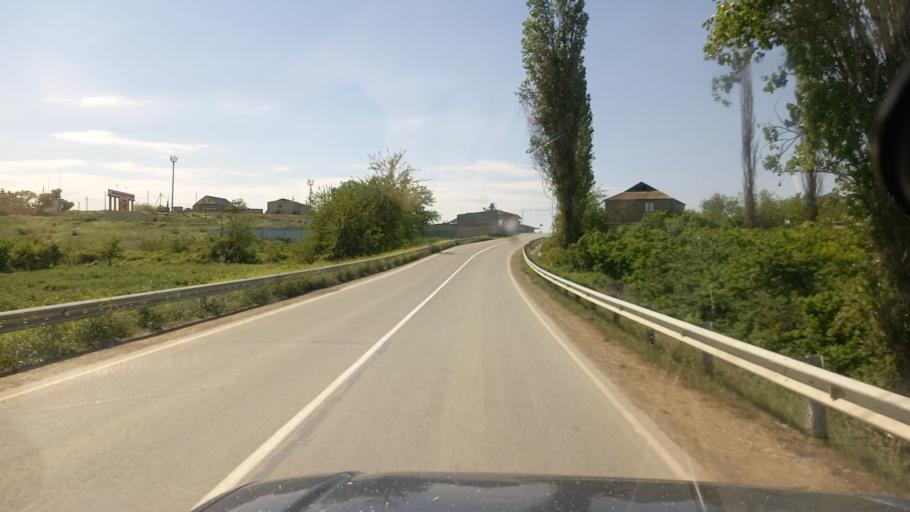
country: RU
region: Dagestan
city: Novaya Maka
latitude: 41.8250
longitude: 48.3907
